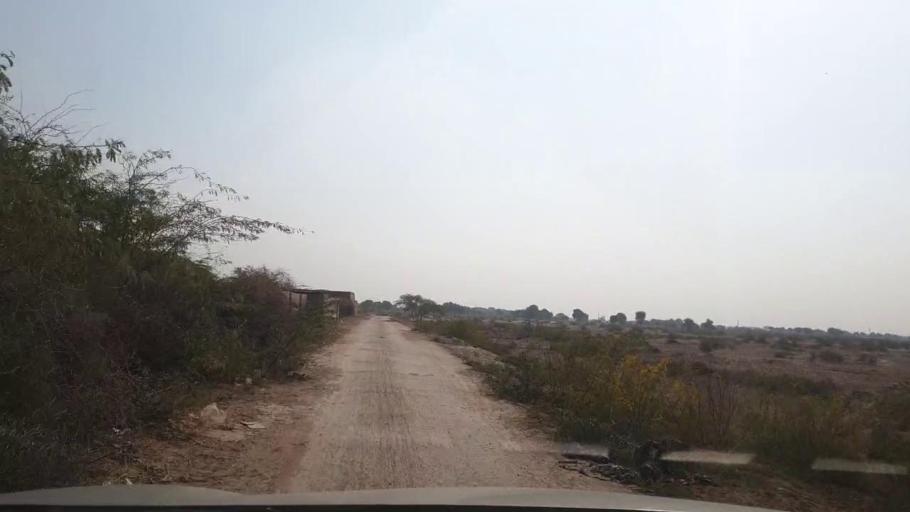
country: PK
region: Sindh
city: Tando Allahyar
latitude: 25.5722
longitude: 68.8181
